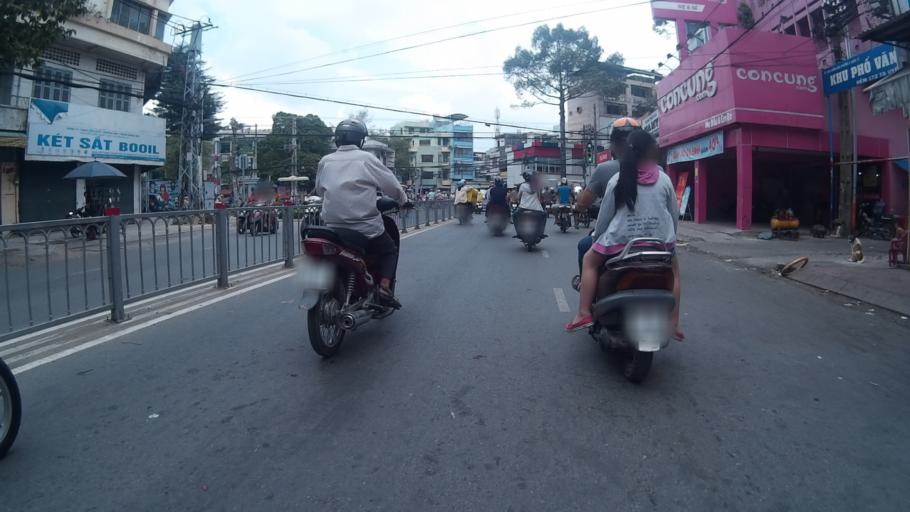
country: VN
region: Ho Chi Minh City
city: Quan Muoi Mot
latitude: 10.7633
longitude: 106.6524
